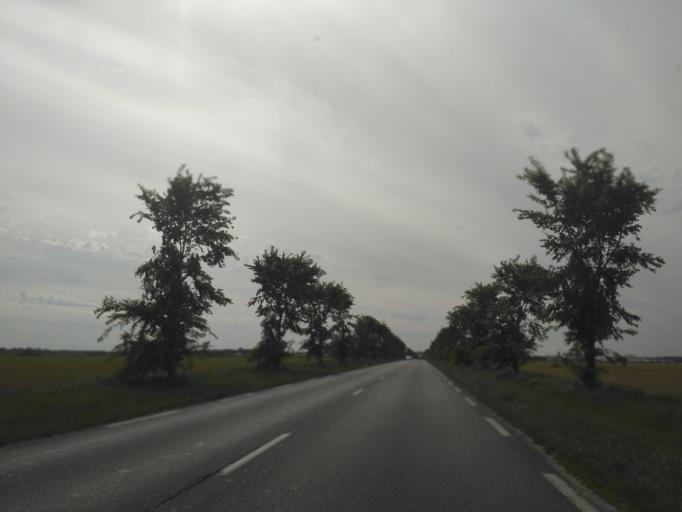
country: FR
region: Ile-de-France
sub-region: Departement de Seine-et-Marne
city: Soignolles-en-Brie
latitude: 48.6320
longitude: 2.6851
